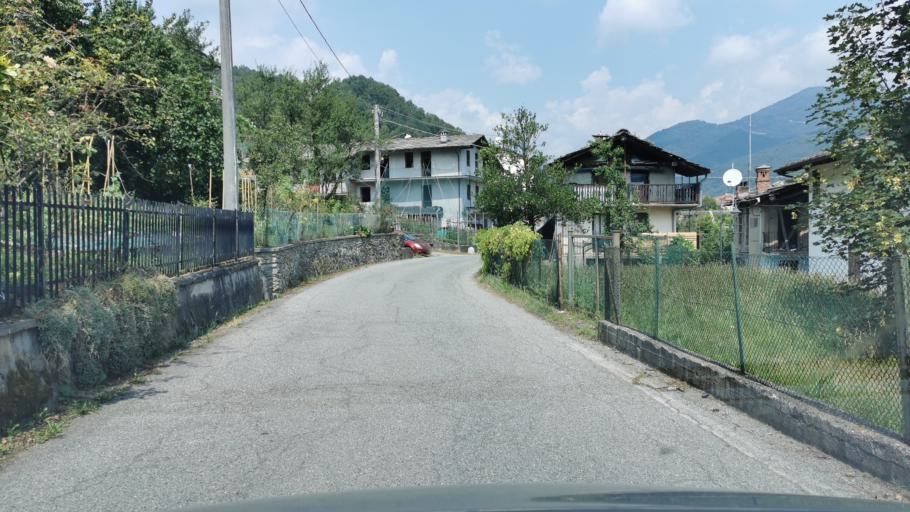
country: IT
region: Piedmont
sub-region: Provincia di Torino
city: La Villa
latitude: 45.2669
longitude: 7.4317
